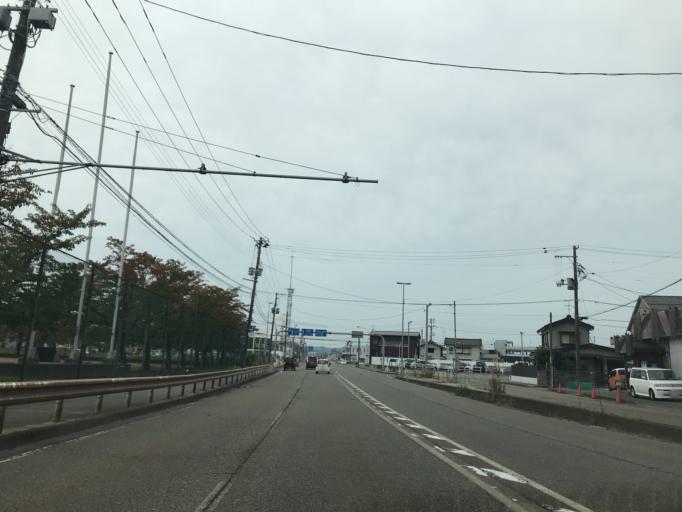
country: JP
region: Niigata
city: Nagaoka
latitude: 37.4259
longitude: 138.8408
